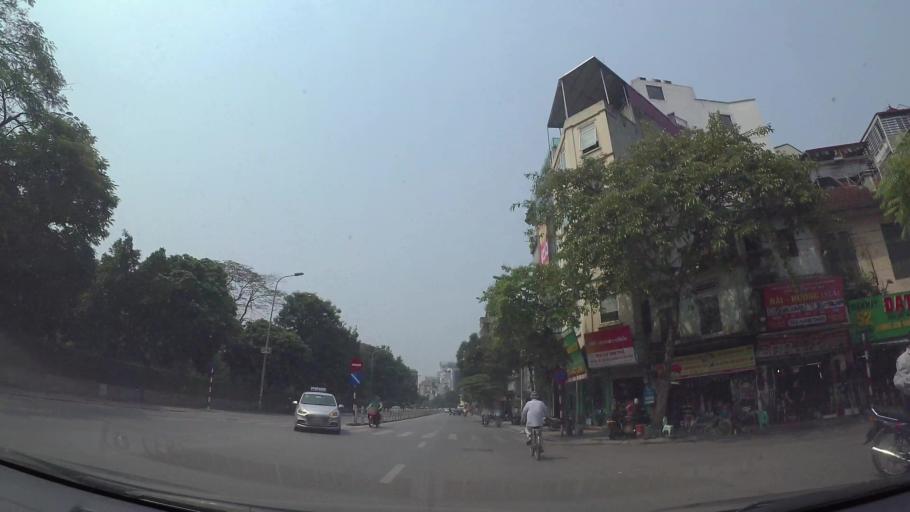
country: VN
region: Ha Noi
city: Hanoi
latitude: 21.0293
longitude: 105.8351
